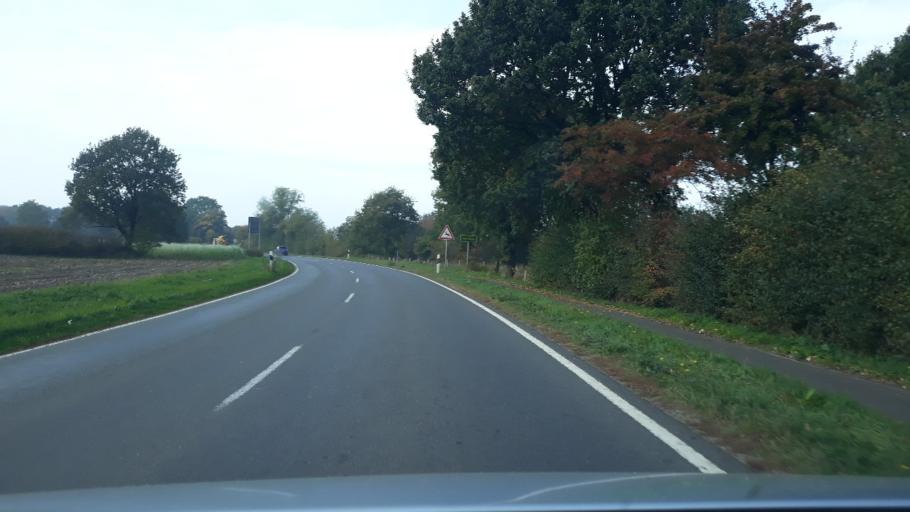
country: DE
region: Schleswig-Holstein
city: Klein Rheide
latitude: 54.4464
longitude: 9.4755
